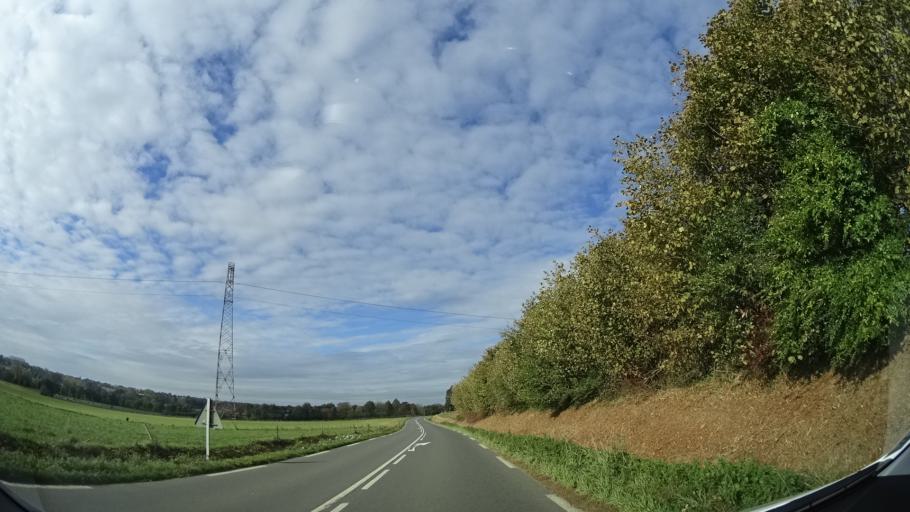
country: FR
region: Brittany
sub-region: Departement d'Ille-et-Vilaine
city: Vignoc
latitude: 48.2425
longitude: -1.8106
